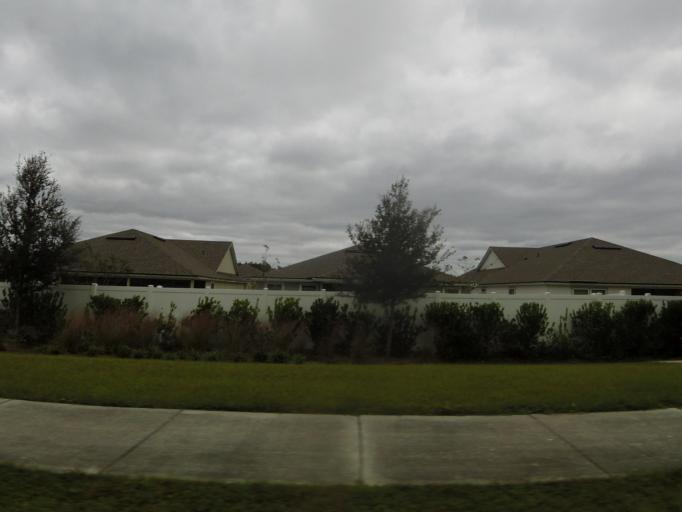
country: US
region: Florida
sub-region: Clay County
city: Lakeside
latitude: 30.1993
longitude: -81.8449
